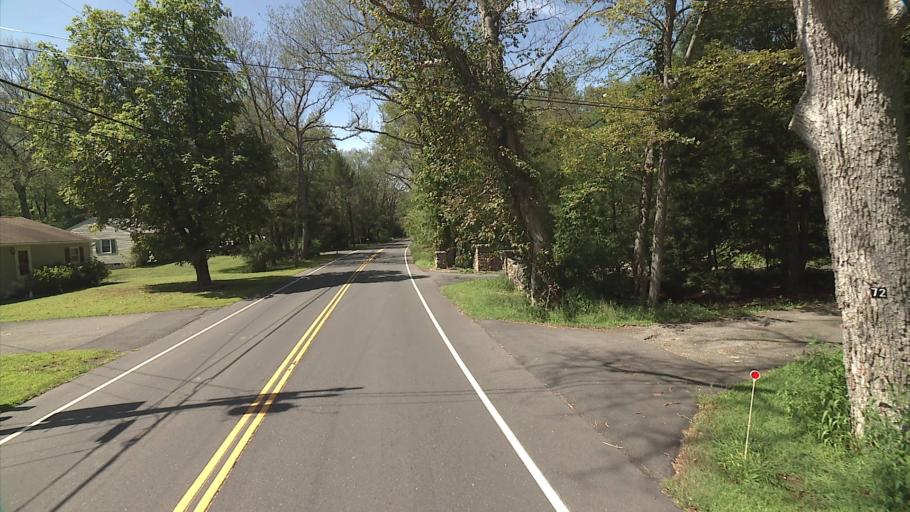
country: US
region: Connecticut
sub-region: New Haven County
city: Middlebury
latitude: 41.5238
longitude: -73.0850
